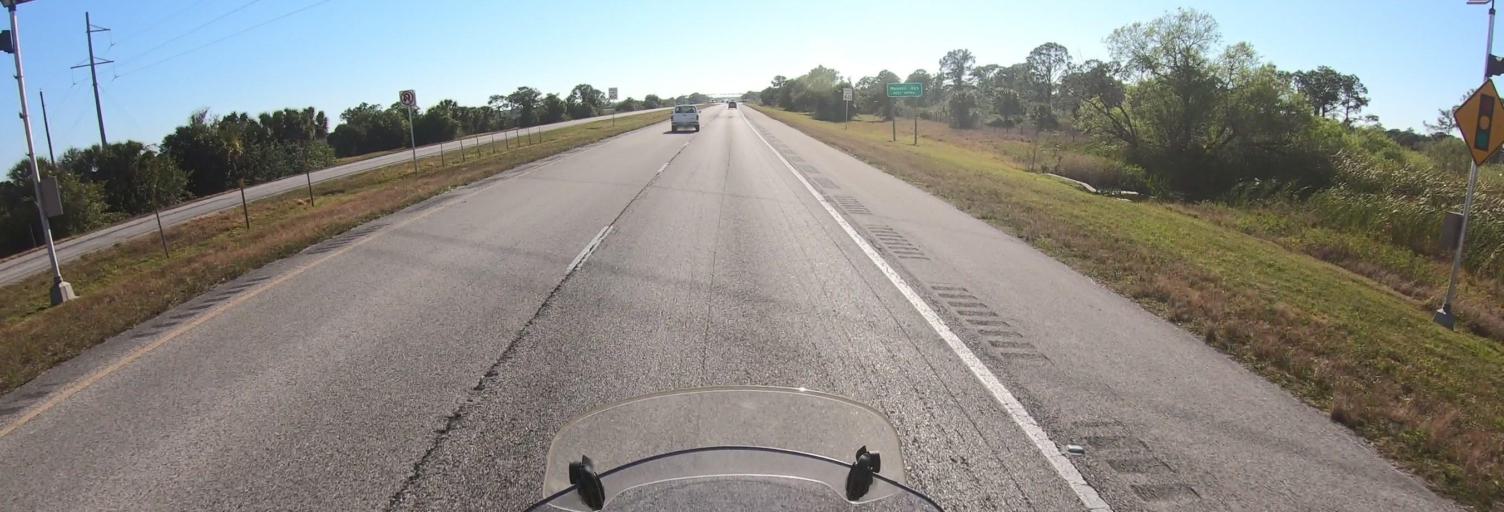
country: US
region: Florida
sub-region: Sarasota County
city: Laurel
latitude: 27.1873
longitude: -82.4418
